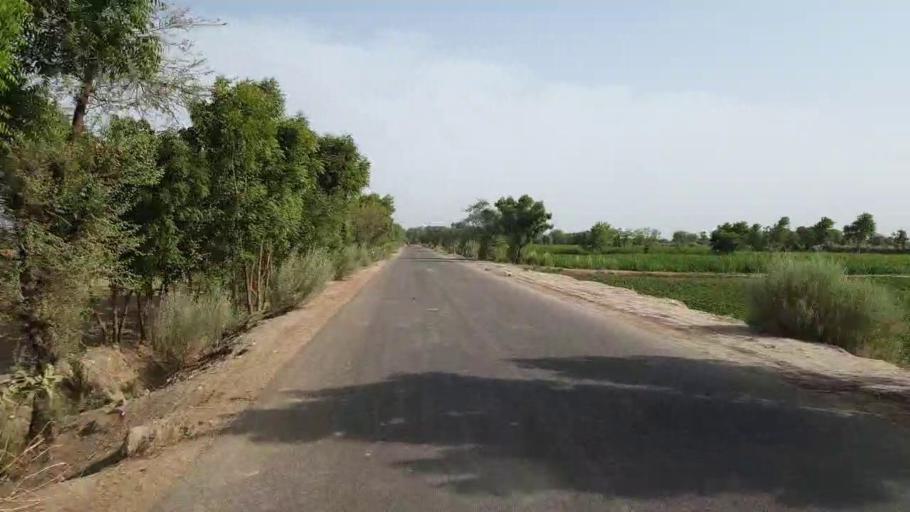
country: PK
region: Sindh
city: Sakrand
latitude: 26.2564
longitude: 68.2848
